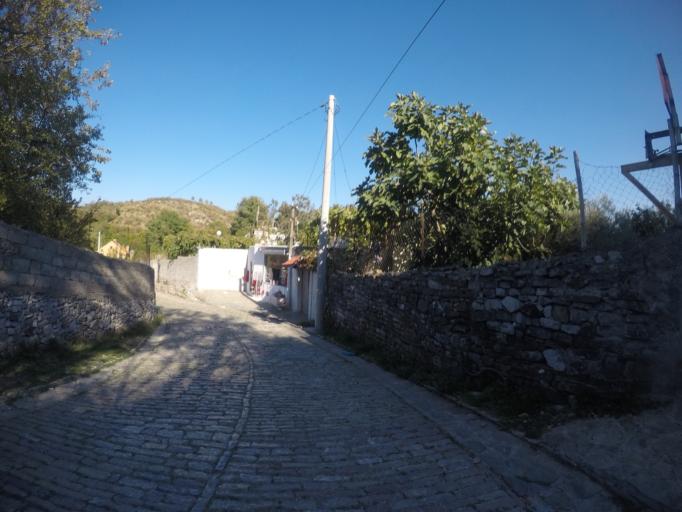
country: AL
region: Shkoder
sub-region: Rrethi i Shkodres
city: Shkoder
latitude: 42.0475
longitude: 19.4961
